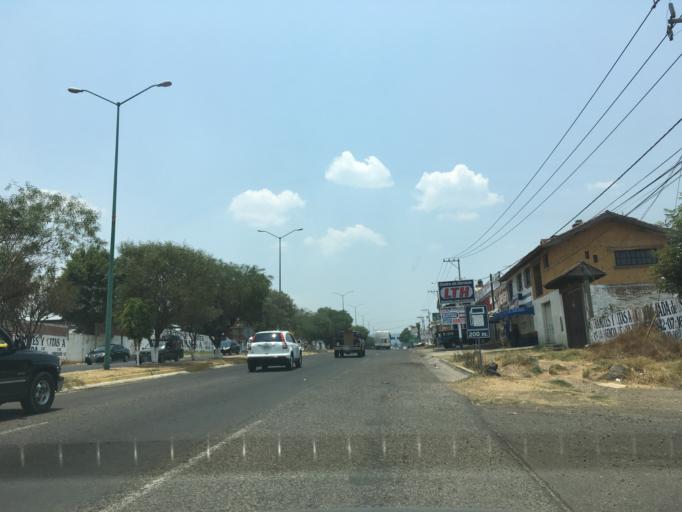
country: MX
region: Michoacan
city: Patzcuaro
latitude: 19.5193
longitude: -101.6169
